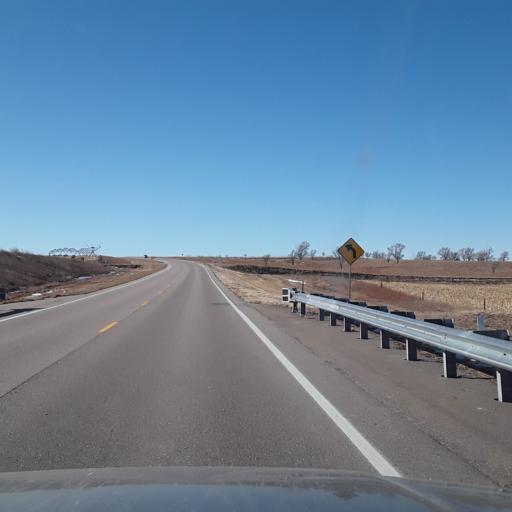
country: US
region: Nebraska
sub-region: Frontier County
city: Stockville
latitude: 40.7058
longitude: -100.2398
